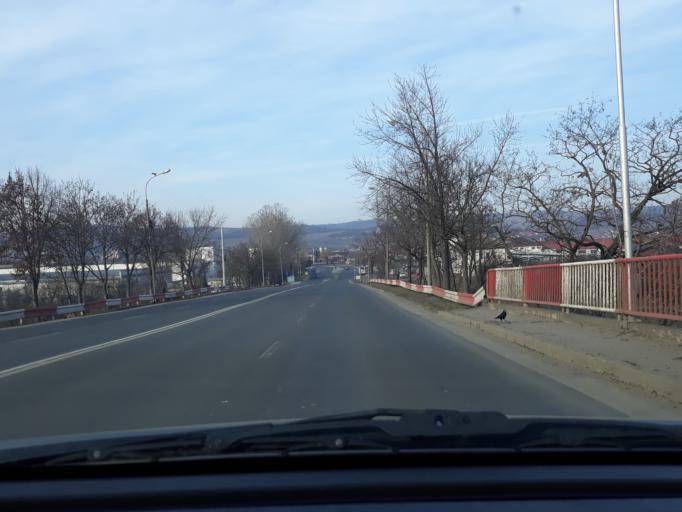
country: RO
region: Salaj
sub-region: Comuna Criseni
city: Criseni
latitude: 47.2180
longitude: 23.0414
